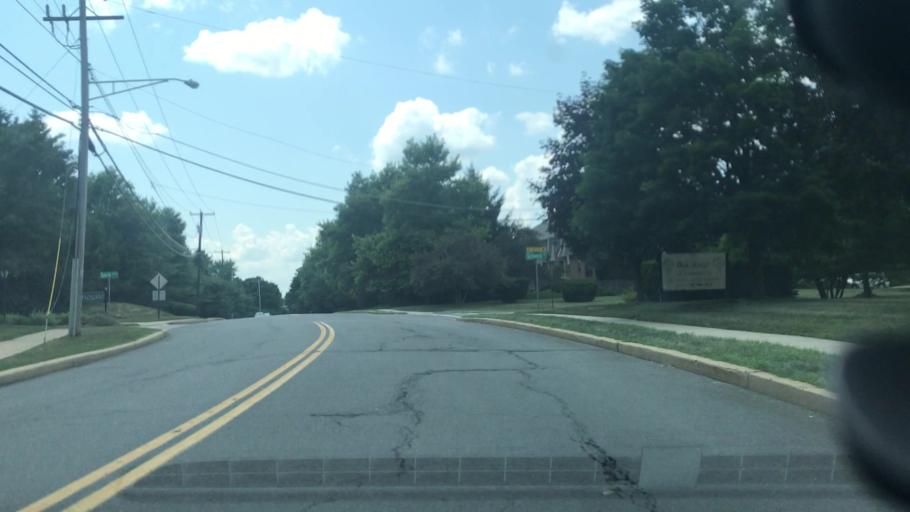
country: US
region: New Jersey
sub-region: Hunterdon County
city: Flemington
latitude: 40.4972
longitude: -74.8460
